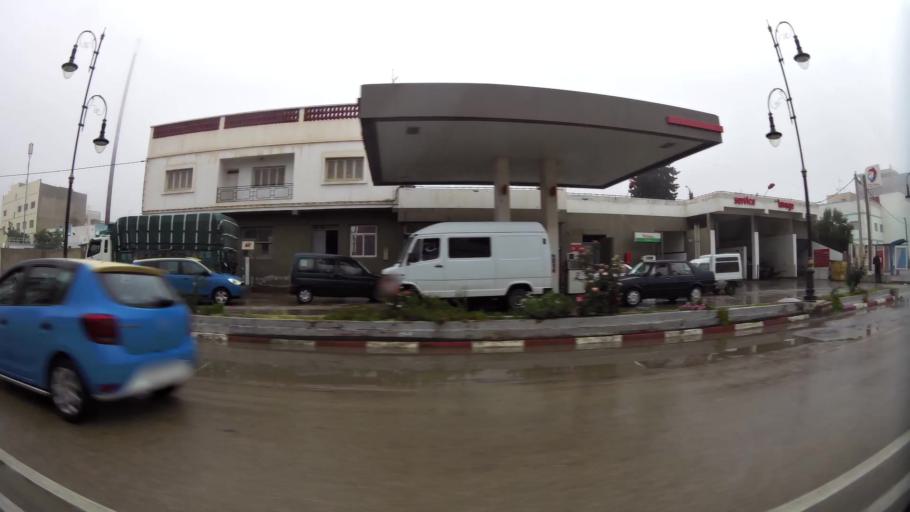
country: MA
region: Taza-Al Hoceima-Taounate
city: Tirhanimine
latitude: 35.1943
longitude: -3.9161
